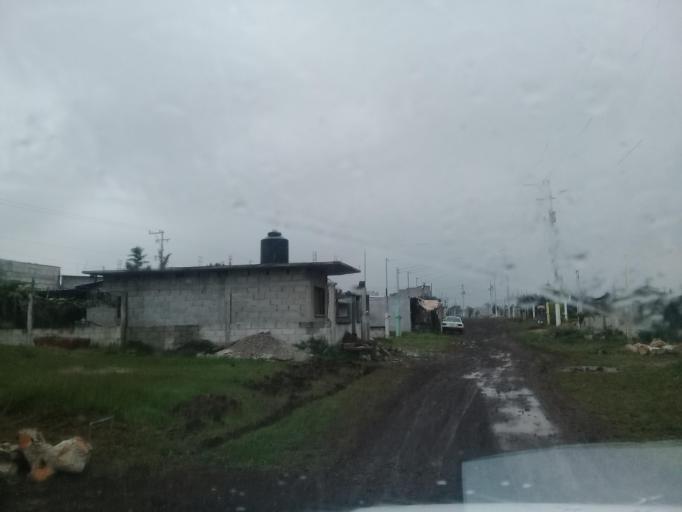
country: MX
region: Veracruz
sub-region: Cordoba
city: San Jose de Tapia
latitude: 18.8502
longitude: -96.9593
